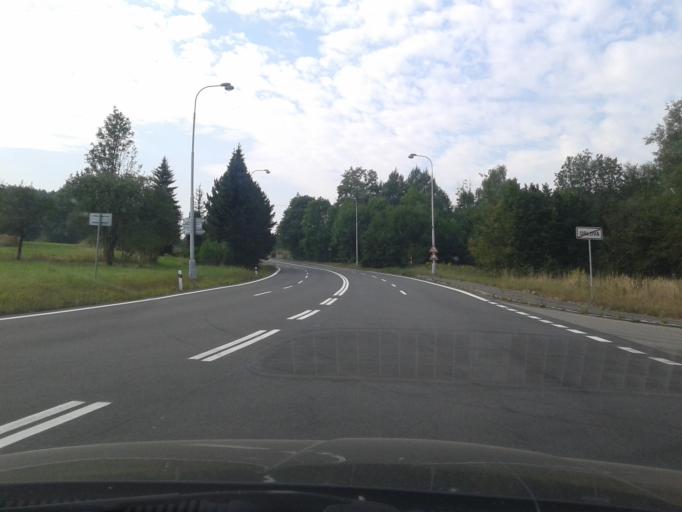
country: CZ
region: Moravskoslezsky
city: Orlova
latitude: 49.8386
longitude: 18.4350
